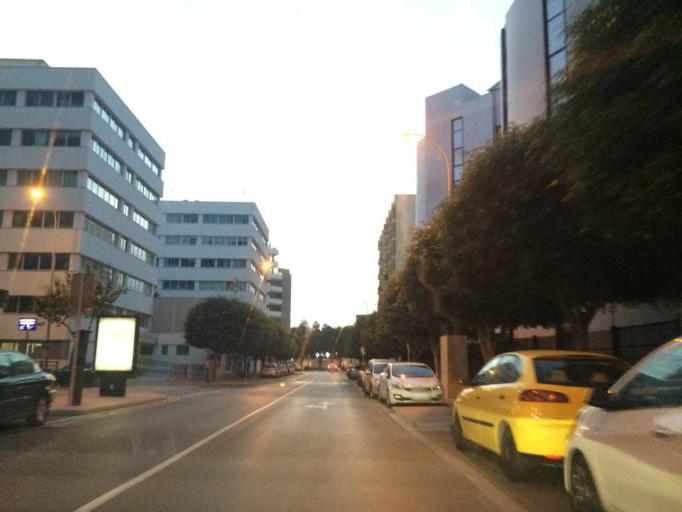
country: ES
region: Andalusia
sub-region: Provincia de Almeria
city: Almeria
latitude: 36.8359
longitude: -2.4600
